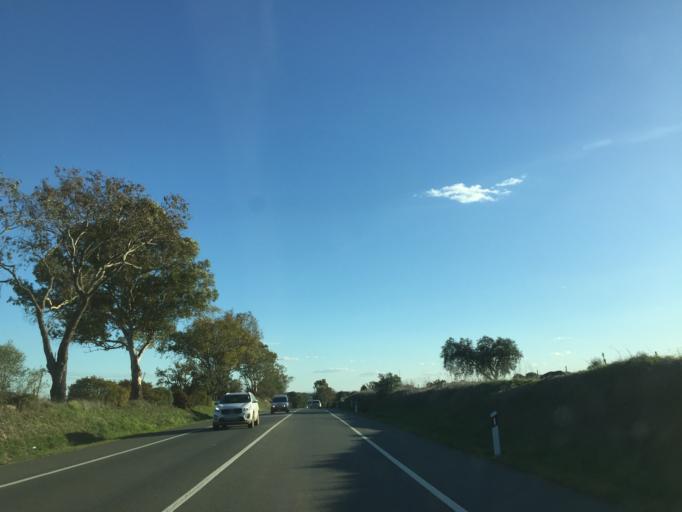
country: PT
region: Setubal
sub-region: Grandola
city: Grandola
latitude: 38.0942
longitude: -8.4185
